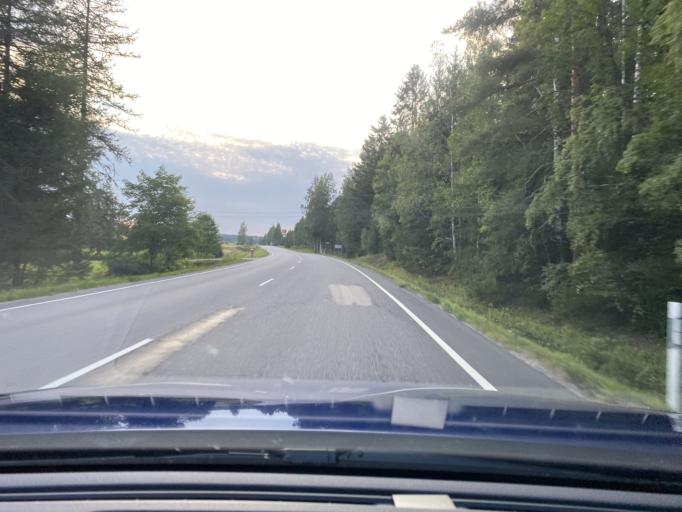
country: FI
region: Satakunta
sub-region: Pohjois-Satakunta
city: Kankaanpaeae
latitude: 61.7828
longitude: 22.4338
